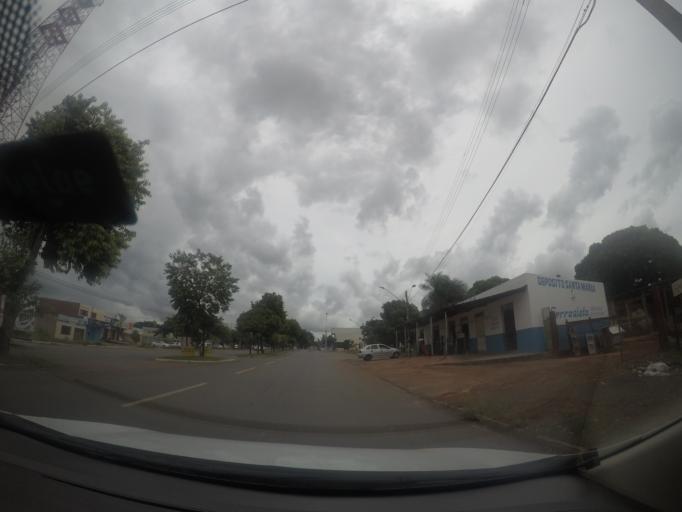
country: BR
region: Goias
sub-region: Trindade
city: Trindade
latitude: -16.6615
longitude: -49.3864
